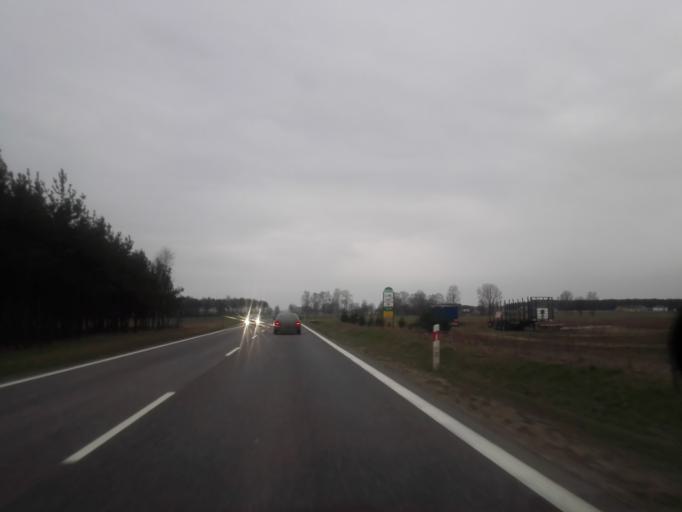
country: PL
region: Podlasie
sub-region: Powiat grajewski
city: Grajewo
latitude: 53.6623
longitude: 22.5239
